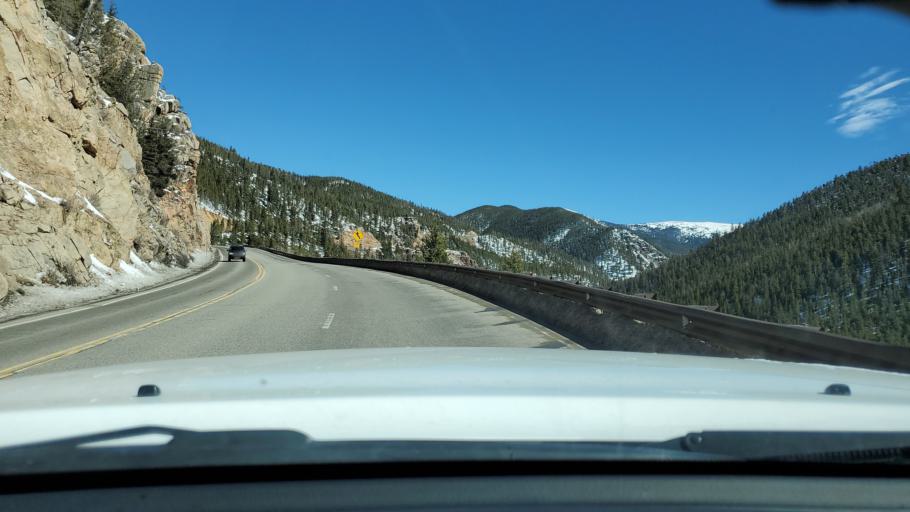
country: US
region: Colorado
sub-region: Chaffee County
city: Salida
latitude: 38.4436
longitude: -106.3585
